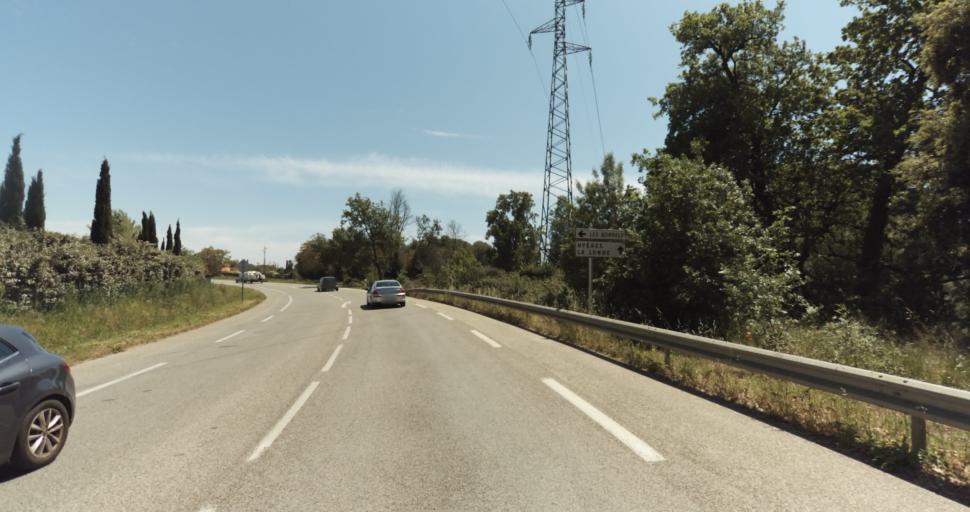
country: FR
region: Provence-Alpes-Cote d'Azur
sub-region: Departement du Var
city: Hyeres
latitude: 43.1460
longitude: 6.1503
